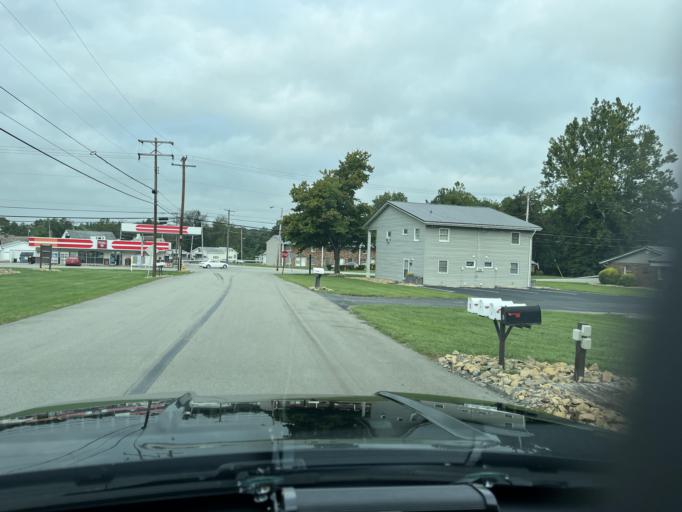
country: US
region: Pennsylvania
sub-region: Fayette County
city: Hopwood
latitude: 39.8648
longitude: -79.7077
